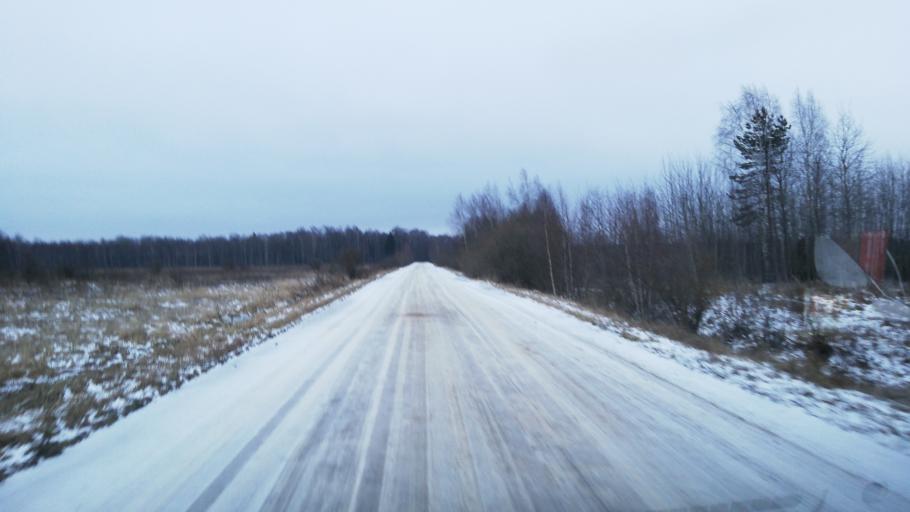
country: RU
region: Kostroma
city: Oktyabr'skiy
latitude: 57.6888
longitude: 41.1762
